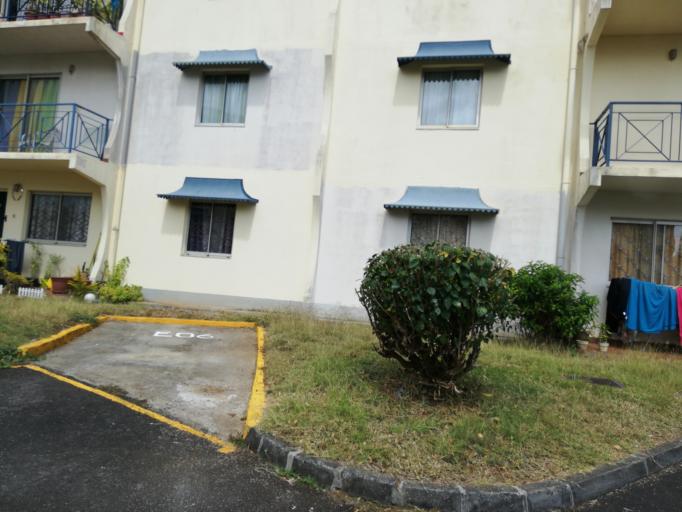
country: MU
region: Moka
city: Moka
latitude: -20.2158
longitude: 57.4759
